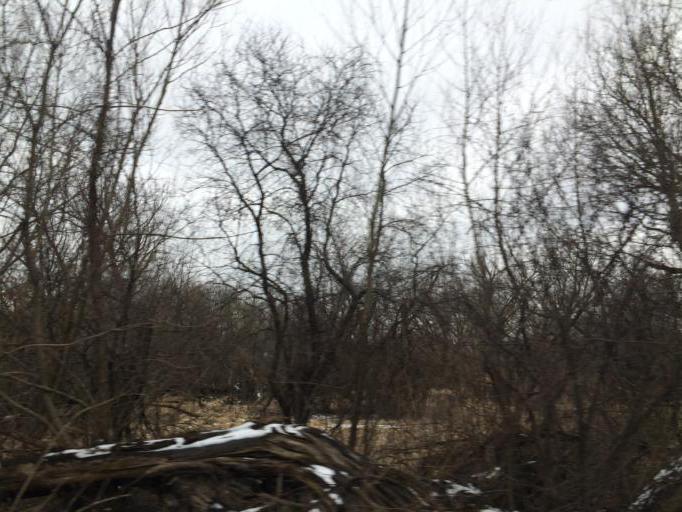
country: US
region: Illinois
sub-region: Cook County
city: Streamwood
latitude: 42.0610
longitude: -88.1698
